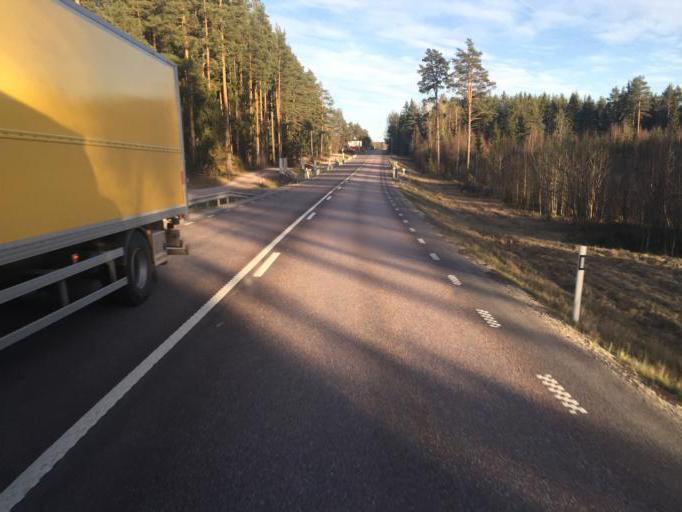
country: SE
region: Dalarna
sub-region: Borlange Kommun
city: Borlaenge
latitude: 60.5277
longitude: 15.3466
